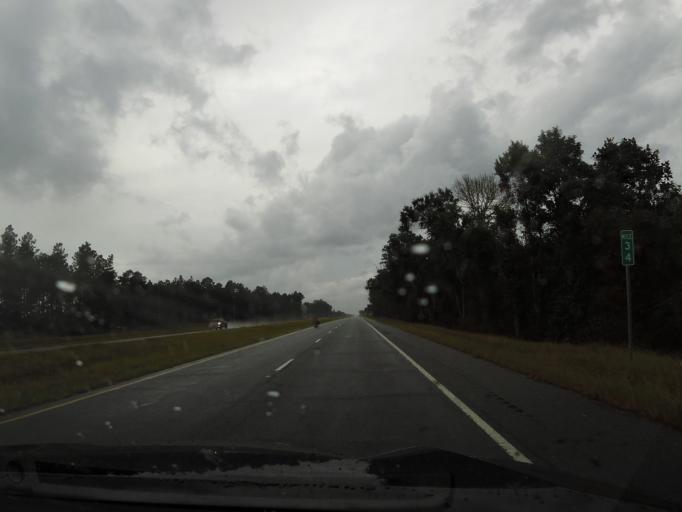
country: US
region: Georgia
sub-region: McIntosh County
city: Darien
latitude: 31.4299
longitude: -81.6740
